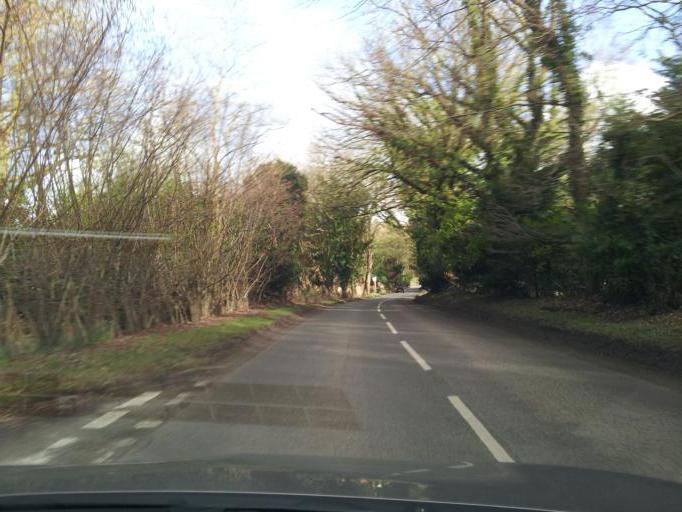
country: GB
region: England
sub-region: Norfolk
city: Horsford
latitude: 52.7278
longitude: 1.2424
